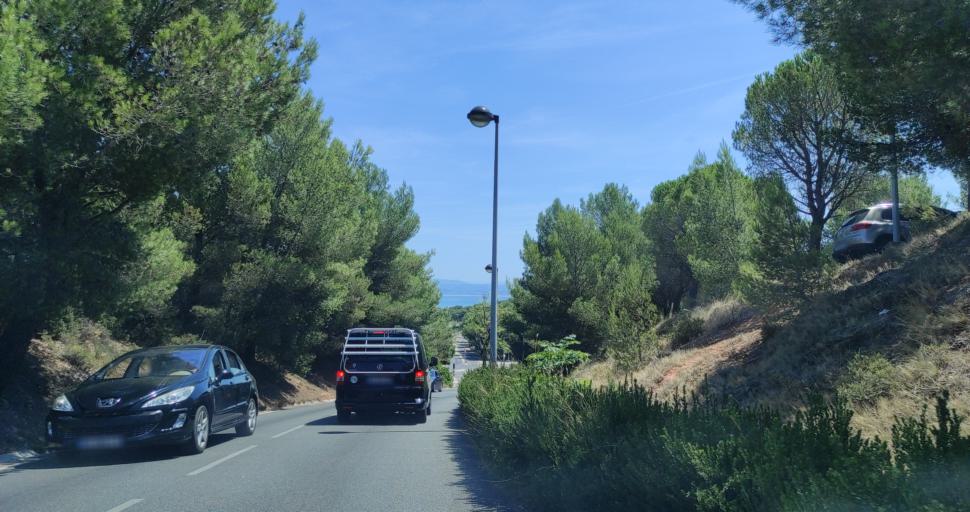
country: FR
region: Provence-Alpes-Cote d'Azur
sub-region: Departement des Bouches-du-Rhone
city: Martigues
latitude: 43.4222
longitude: 5.0487
